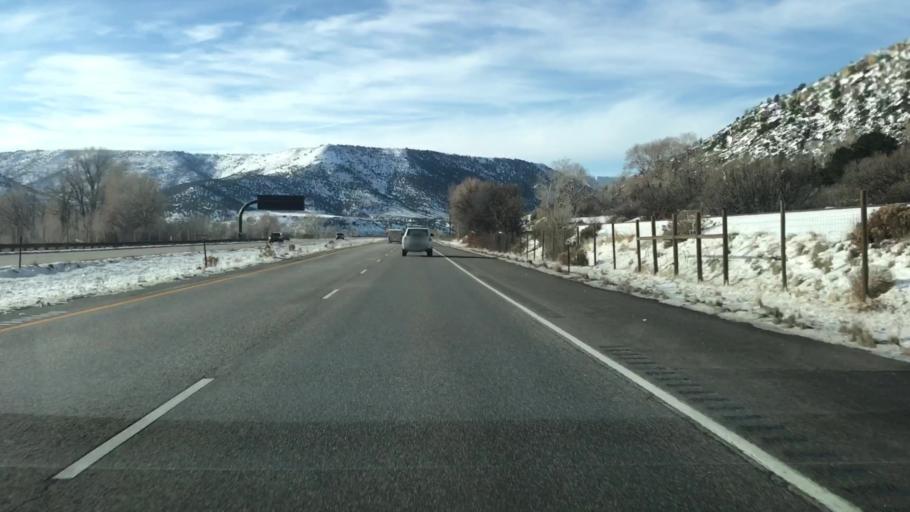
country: US
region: Colorado
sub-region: Garfield County
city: New Castle
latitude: 39.5648
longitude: -107.5499
